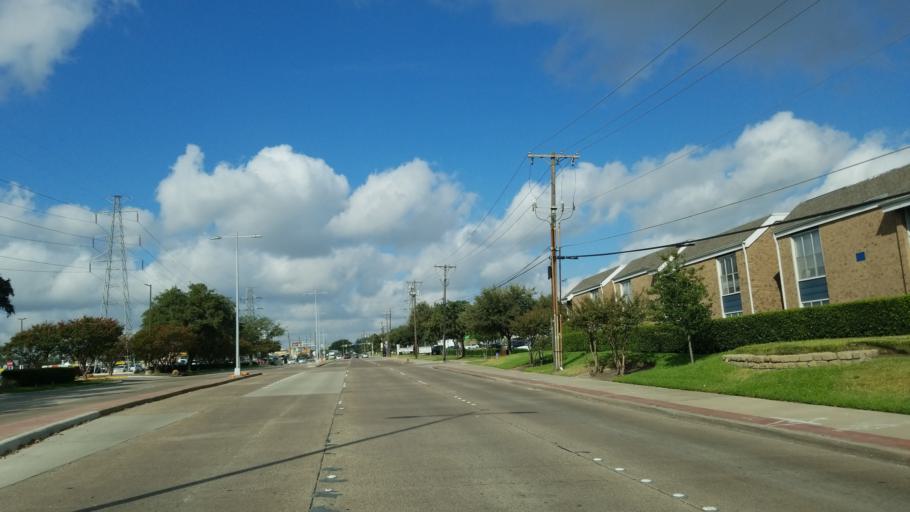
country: US
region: Texas
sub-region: Dallas County
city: Richardson
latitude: 32.9400
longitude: -96.7656
